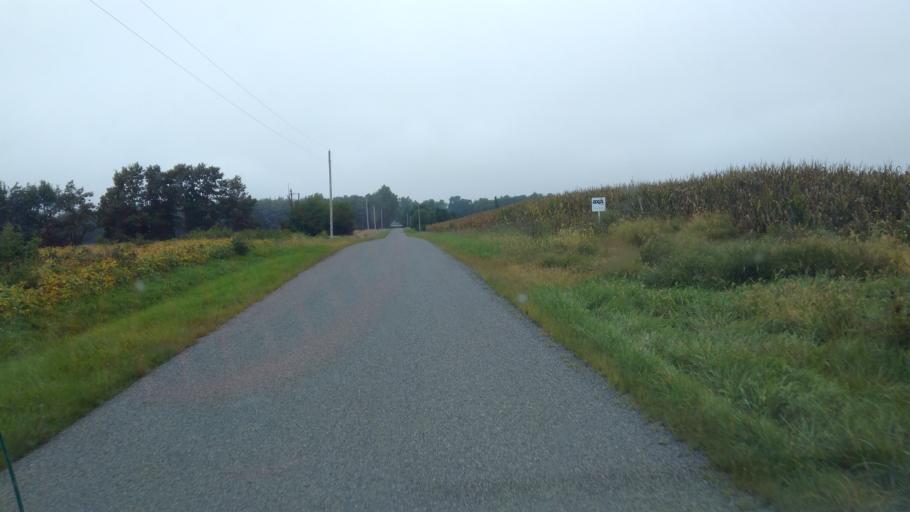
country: US
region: Ohio
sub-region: Logan County
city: Northwood
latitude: 40.4611
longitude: -83.5677
